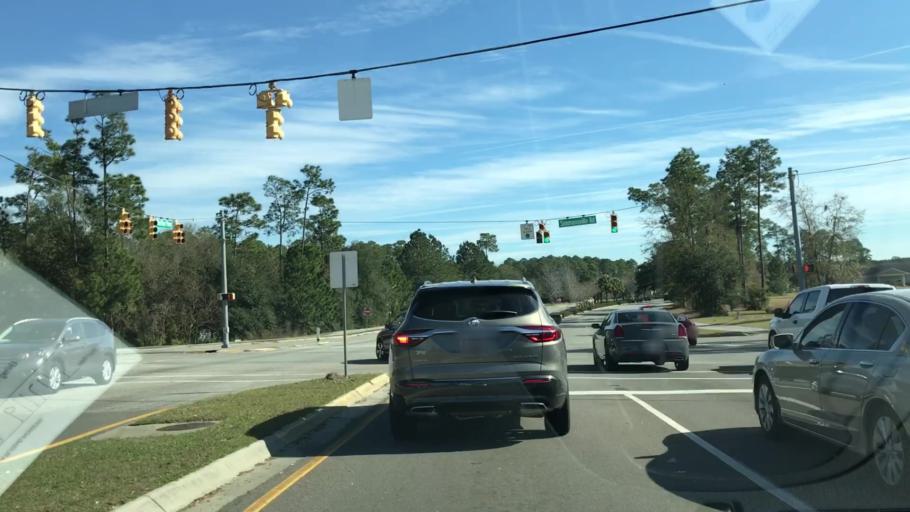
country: US
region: South Carolina
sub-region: Beaufort County
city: Bluffton
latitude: 32.2621
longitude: -80.8712
